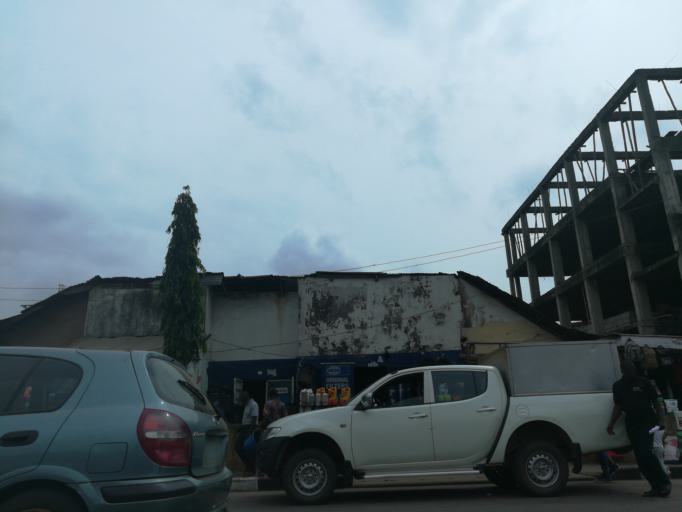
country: NG
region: Lagos
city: Ikeja
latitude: 6.6013
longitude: 3.3638
